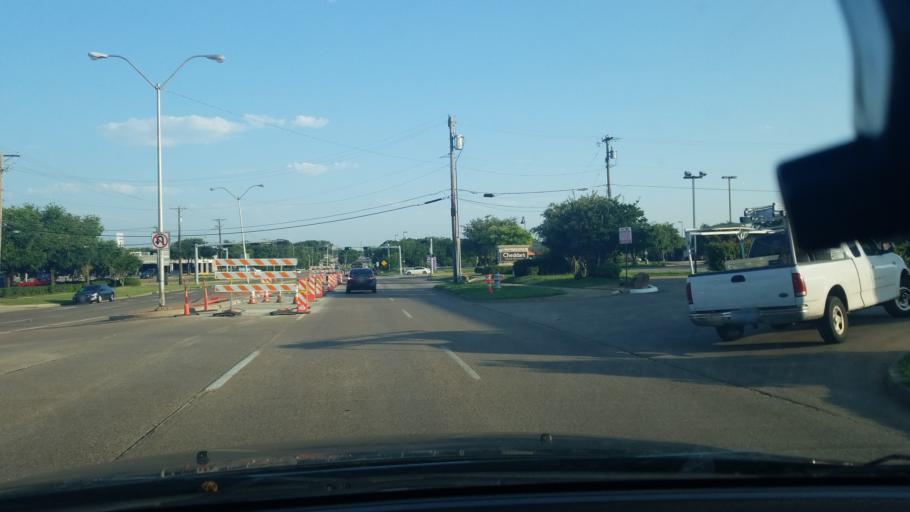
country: US
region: Texas
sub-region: Dallas County
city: Mesquite
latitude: 32.7824
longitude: -96.6257
